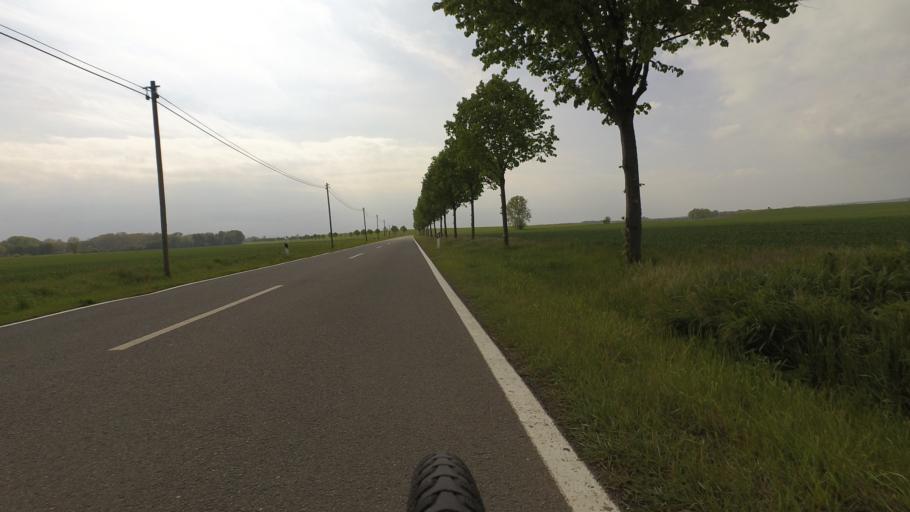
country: DE
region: Saxony-Anhalt
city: Langenstein
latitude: 51.8924
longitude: 10.9809
